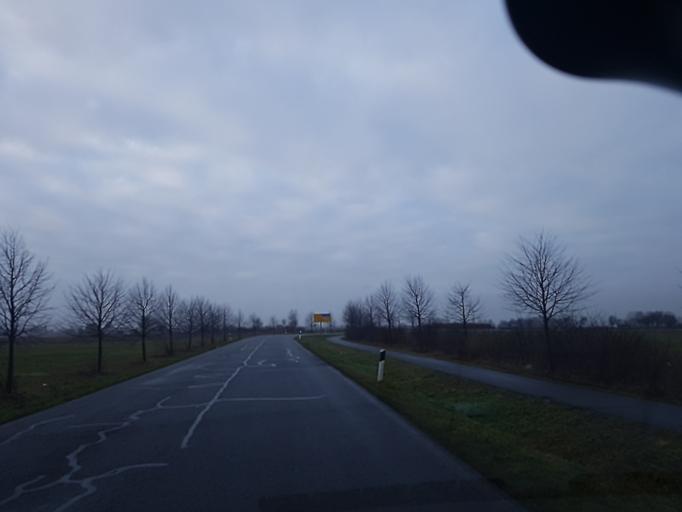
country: DE
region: Brandenburg
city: Finsterwalde
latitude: 51.6078
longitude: 13.7177
